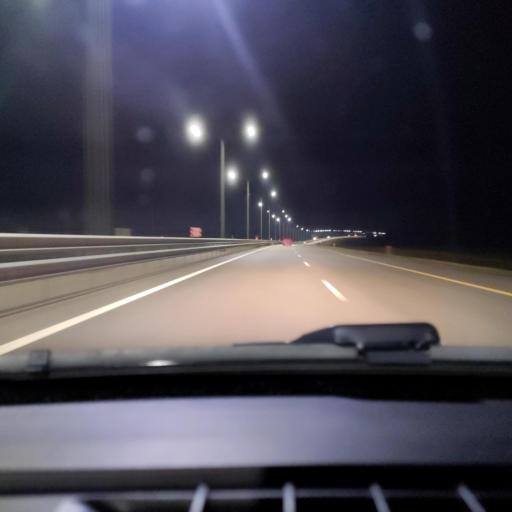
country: RU
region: Voronezj
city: Podkletnoye
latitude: 51.5331
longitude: 39.5075
